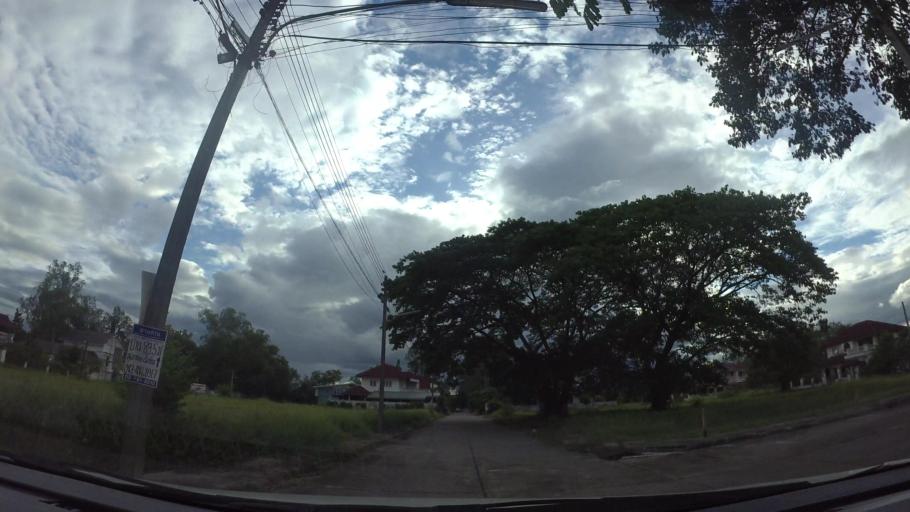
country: TH
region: Chiang Mai
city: Saraphi
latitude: 18.7410
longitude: 99.0304
